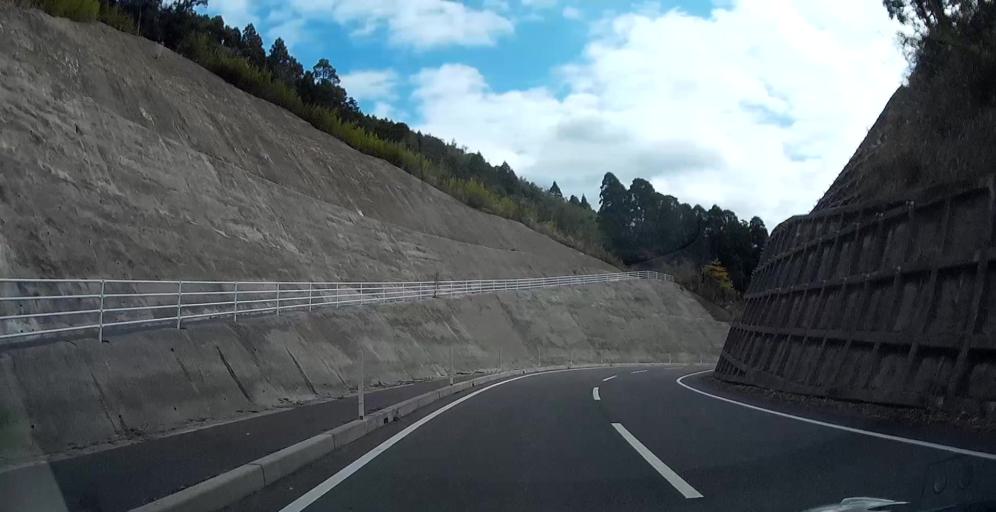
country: JP
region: Kumamoto
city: Minamata
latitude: 32.2319
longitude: 130.4259
